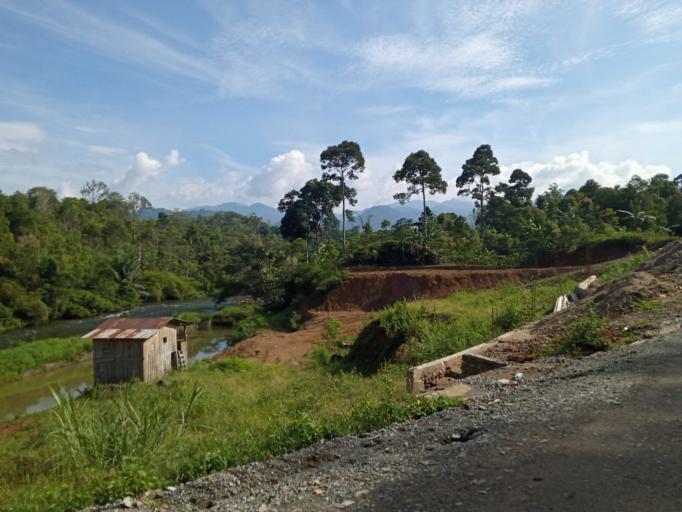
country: ID
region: Jambi
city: Sungai Penuh
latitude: -2.1461
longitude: 101.5684
